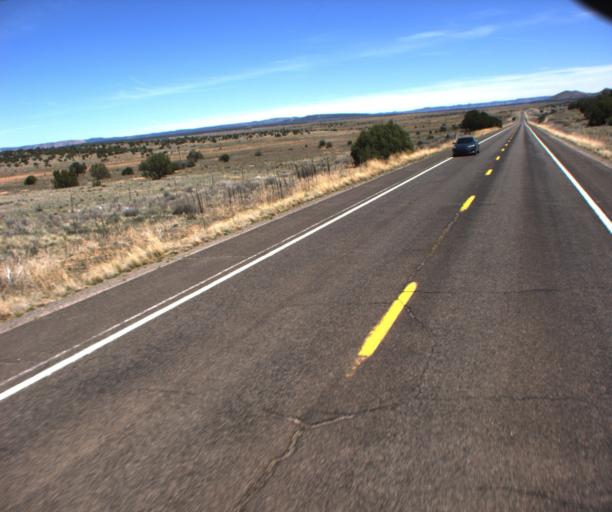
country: US
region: Arizona
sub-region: Mohave County
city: Peach Springs
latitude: 35.5523
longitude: -113.3502
